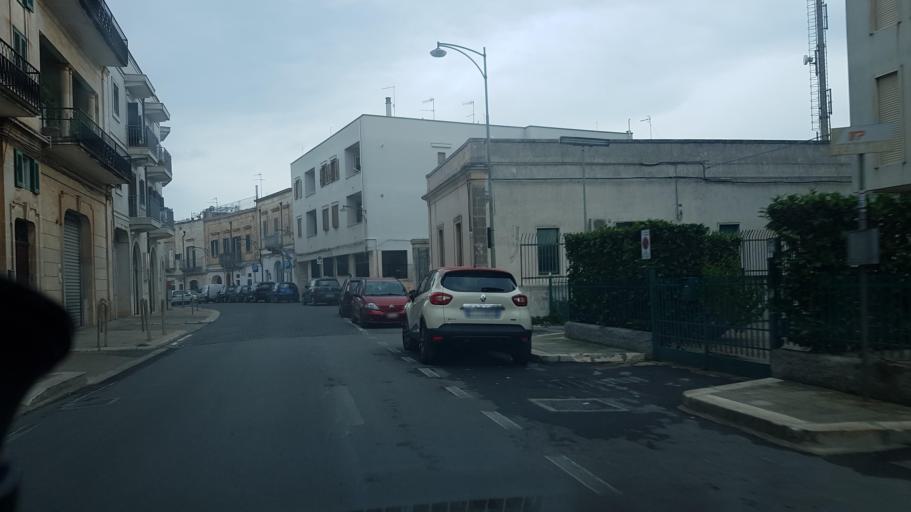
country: IT
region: Apulia
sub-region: Provincia di Brindisi
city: Ostuni
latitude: 40.7288
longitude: 17.5846
